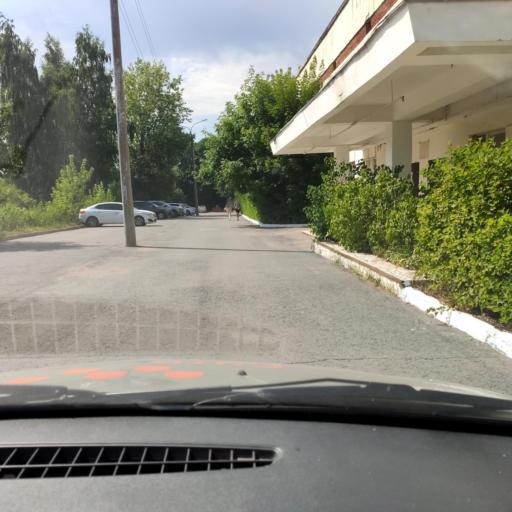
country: RU
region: Bashkortostan
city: Ufa
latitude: 54.7378
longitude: 56.0139
